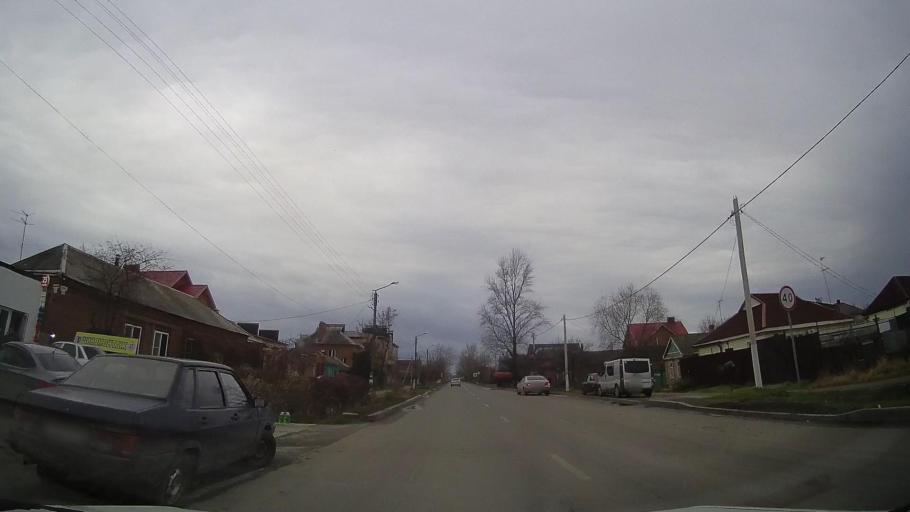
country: RU
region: Rostov
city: Bataysk
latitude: 47.1263
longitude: 39.7435
